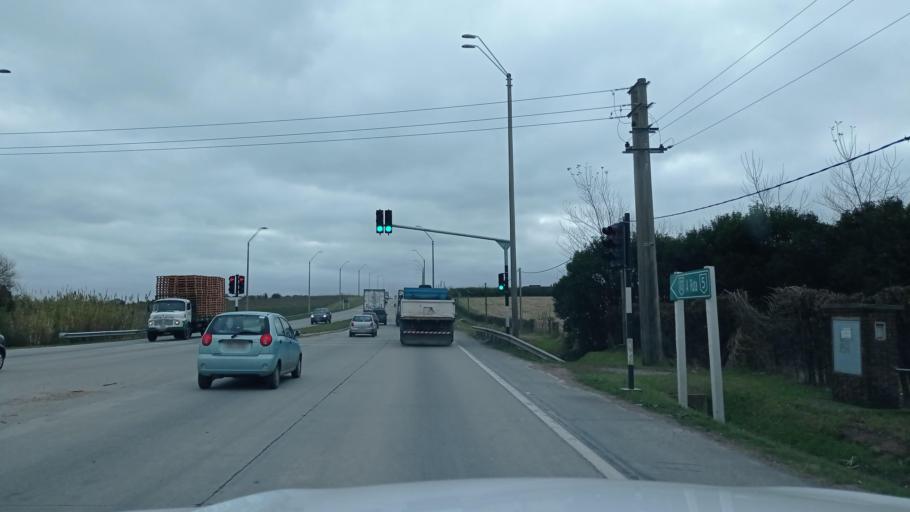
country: UY
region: Canelones
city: La Paz
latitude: -34.7911
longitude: -56.2106
